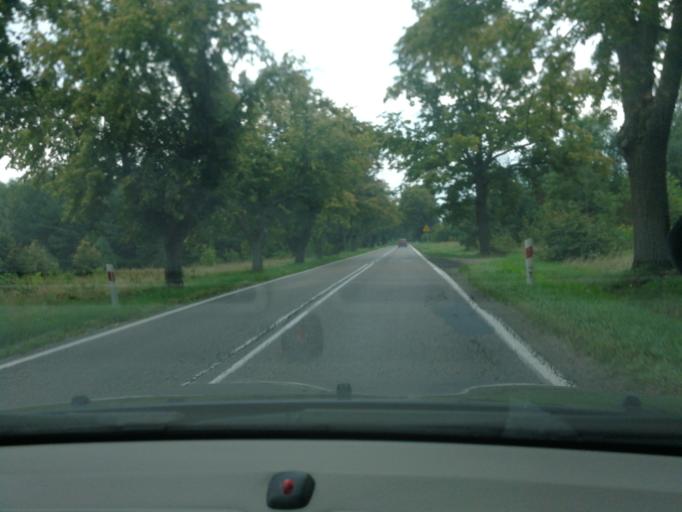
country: PL
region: Masovian Voivodeship
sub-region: Powiat zyrardowski
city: Radziejowice
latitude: 52.0346
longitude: 20.5760
